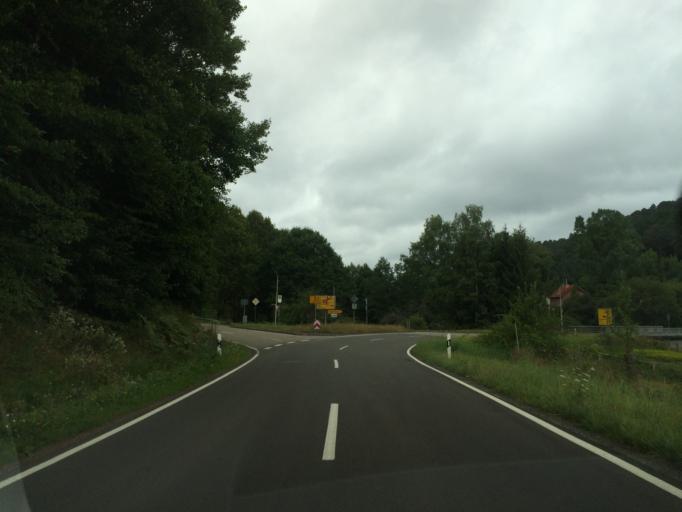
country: DE
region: Rheinland-Pfalz
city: Ruppertsweiler
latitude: 49.1682
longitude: 7.7183
